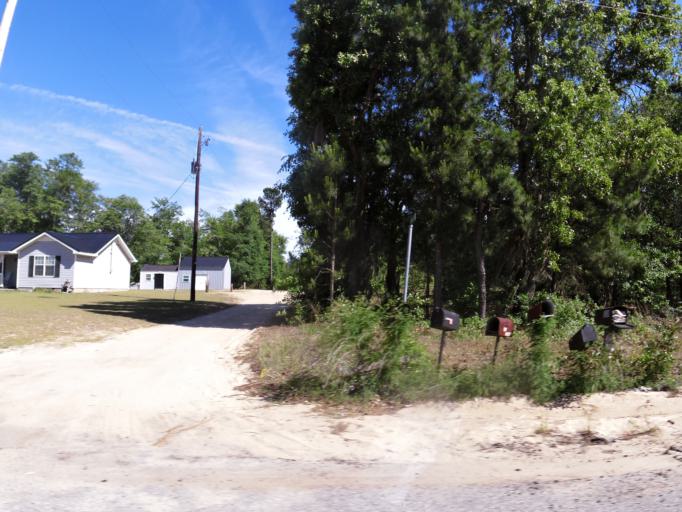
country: US
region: South Carolina
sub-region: Barnwell County
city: Blackville
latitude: 33.3466
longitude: -81.2344
